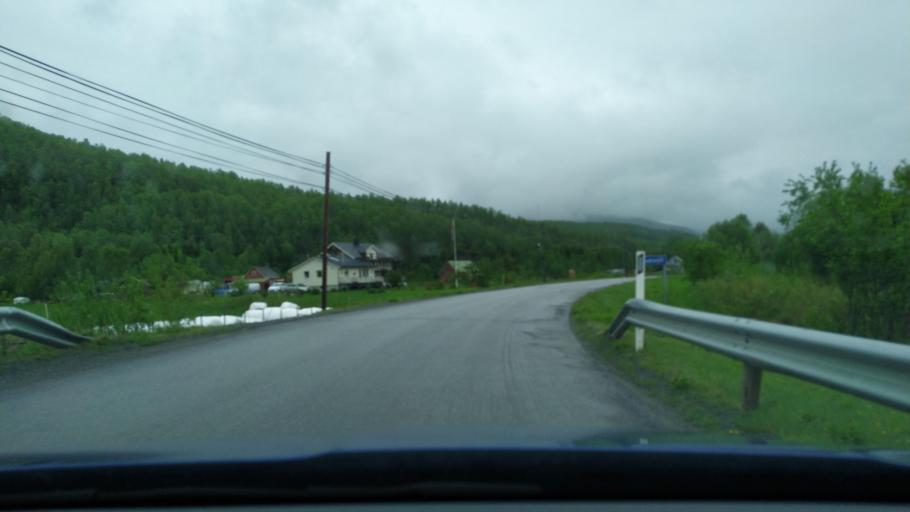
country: NO
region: Troms
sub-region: Dyroy
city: Brostadbotn
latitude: 69.0712
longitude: 17.7333
